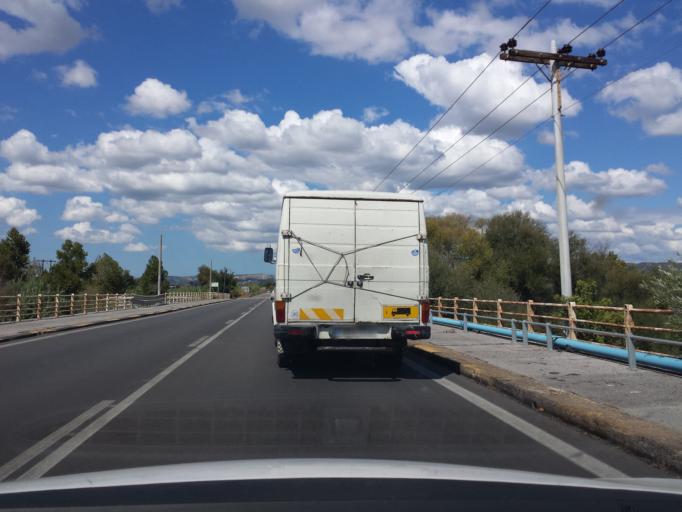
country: GR
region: West Greece
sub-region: Nomos Ileias
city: Epitalion
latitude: 37.6426
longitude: 21.4765
